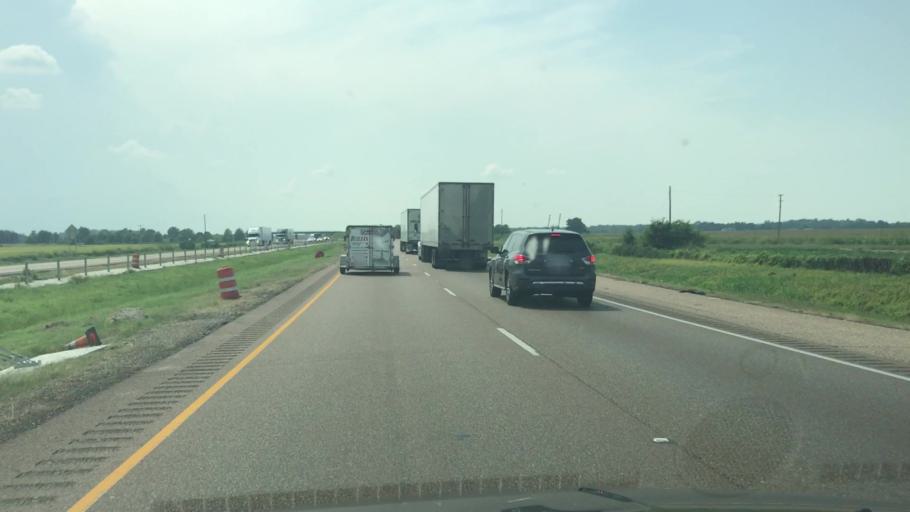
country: US
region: Arkansas
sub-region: Crittenden County
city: Earle
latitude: 35.1513
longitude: -90.3920
